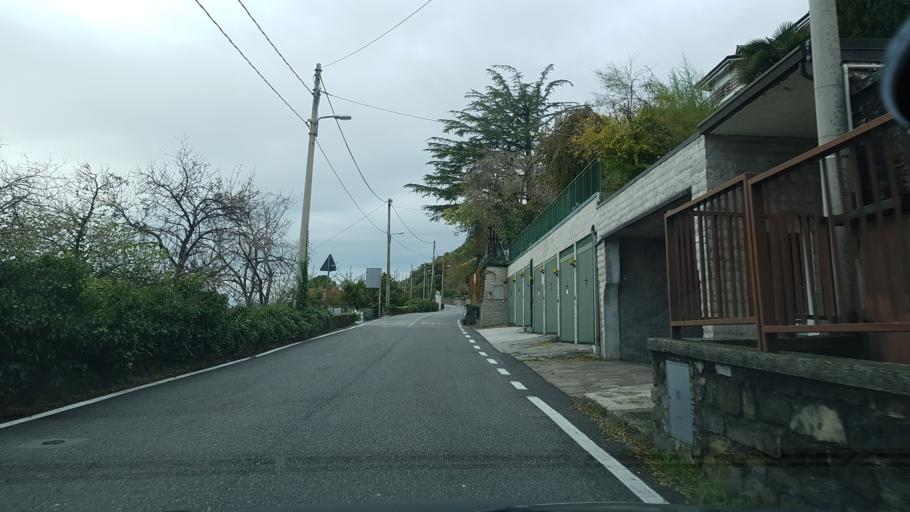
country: IT
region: Friuli Venezia Giulia
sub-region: Provincia di Trieste
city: Prosecco-Contovello
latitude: 45.6878
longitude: 13.7525
